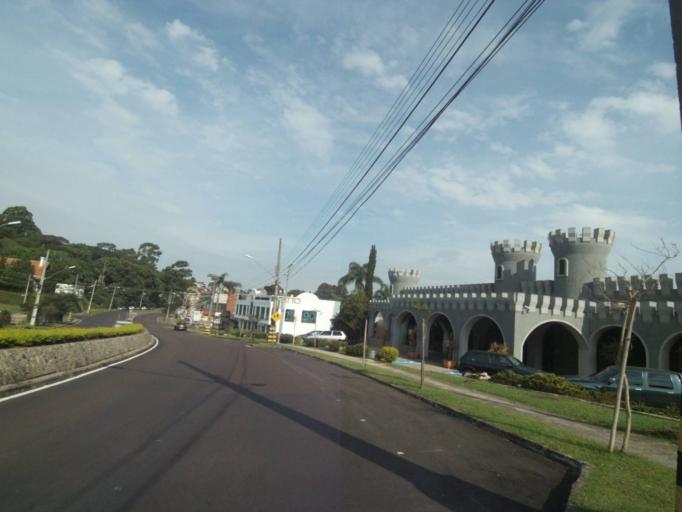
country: BR
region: Parana
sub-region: Curitiba
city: Curitiba
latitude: -25.4133
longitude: -49.3168
